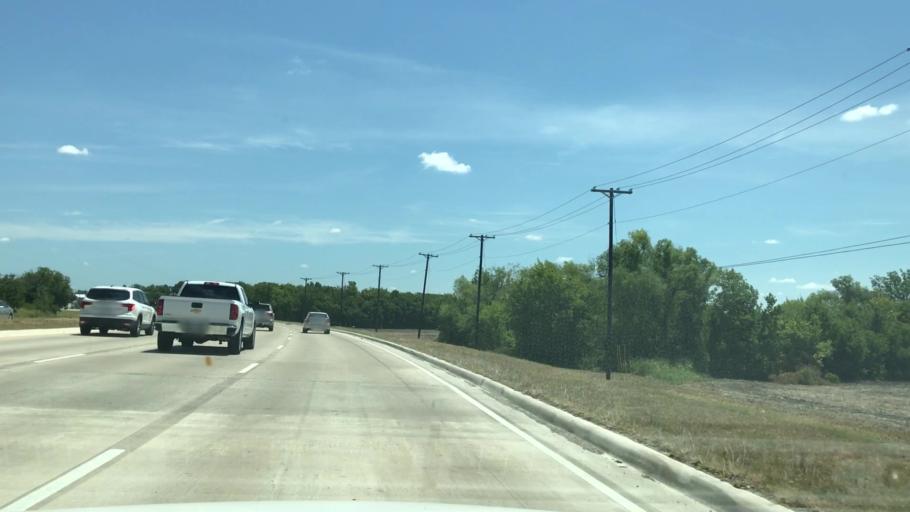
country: US
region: Texas
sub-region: Collin County
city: Lavon
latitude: 33.0219
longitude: -96.4716
